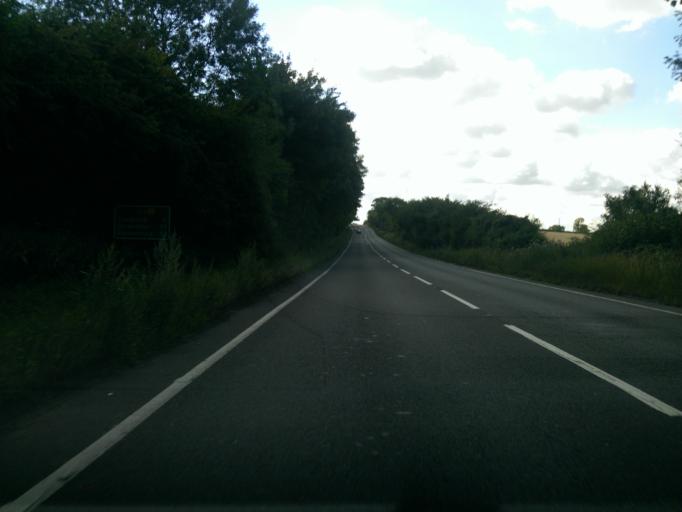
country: GB
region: England
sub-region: Warwickshire
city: Atherstone
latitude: 52.5823
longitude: -1.5631
